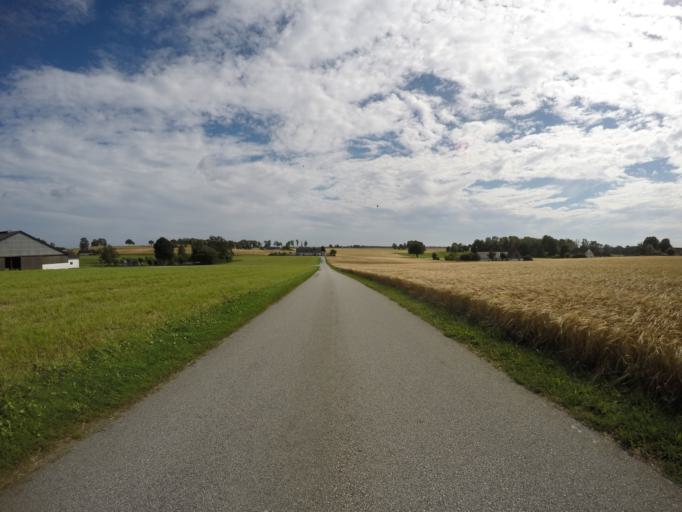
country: SE
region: Skane
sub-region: Simrishamns Kommun
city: Simrishamn
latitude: 55.4928
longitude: 14.2574
